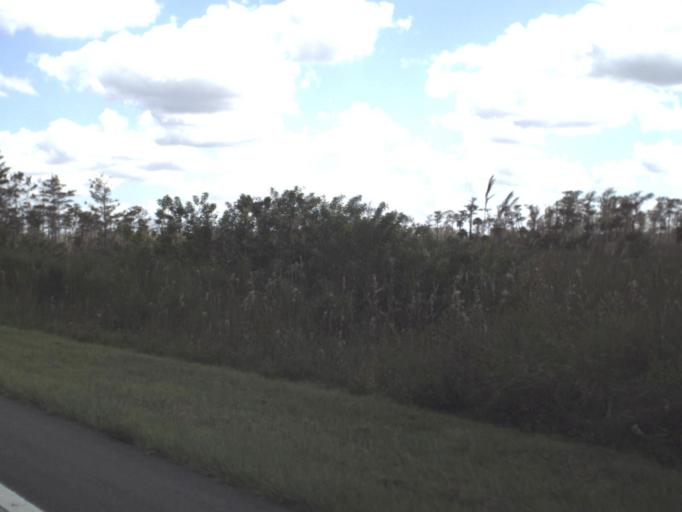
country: US
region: Florida
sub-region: Collier County
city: Marco
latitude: 25.8753
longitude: -81.2150
